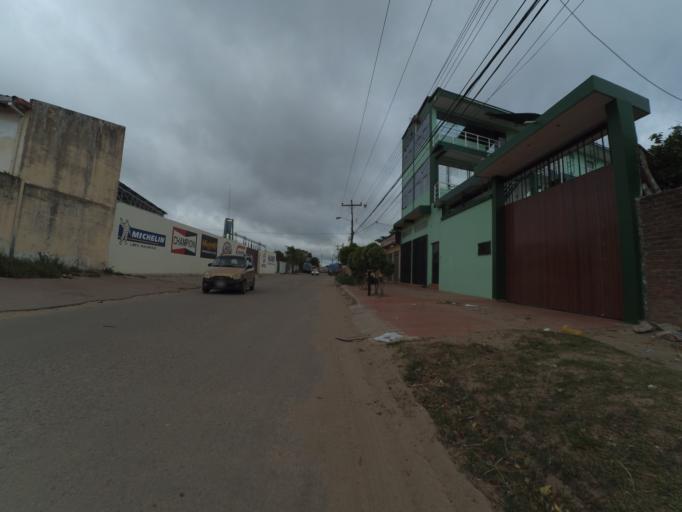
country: BO
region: Santa Cruz
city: Santa Cruz de la Sierra
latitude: -17.8127
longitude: -63.2123
